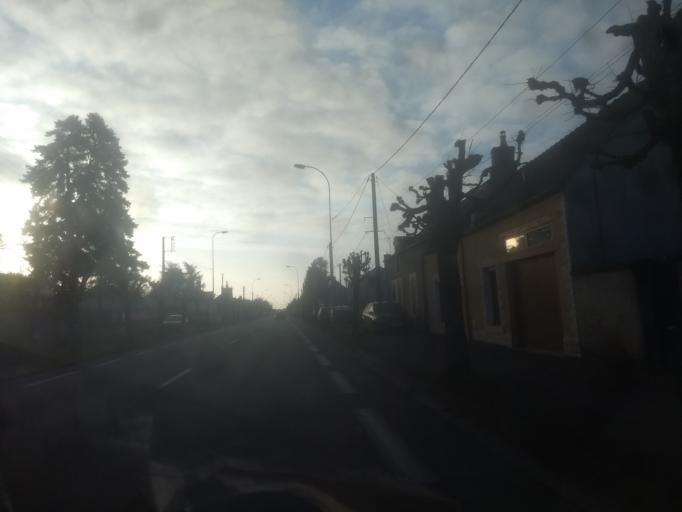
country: FR
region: Centre
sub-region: Departement du Cher
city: Mehun-sur-Yevre
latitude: 47.1513
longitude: 2.2143
